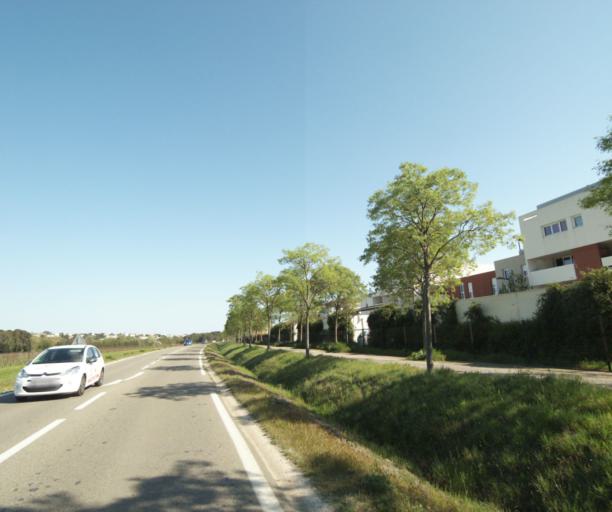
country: FR
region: Languedoc-Roussillon
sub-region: Departement de l'Herault
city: Jacou
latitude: 43.6679
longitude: 3.9196
